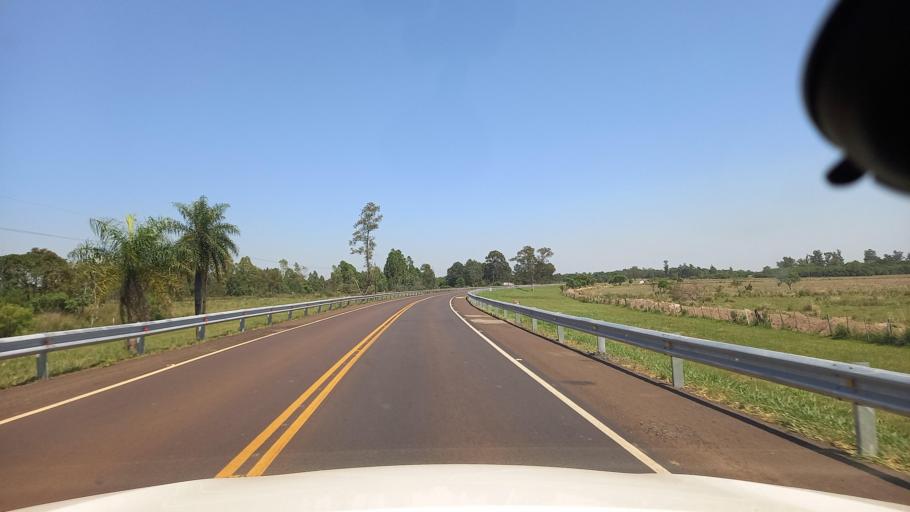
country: PY
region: Itapua
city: General Delgado
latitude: -27.1107
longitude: -56.4215
